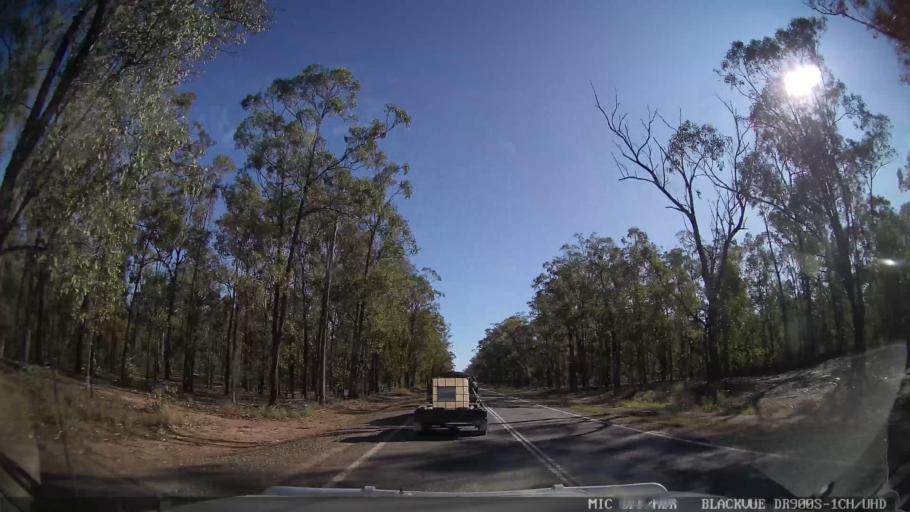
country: AU
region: Queensland
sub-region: Bundaberg
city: Childers
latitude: -25.2164
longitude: 152.0735
